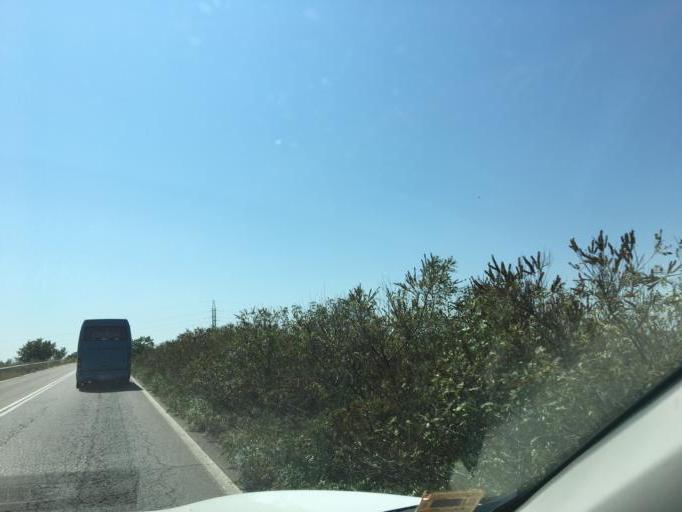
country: BG
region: Burgas
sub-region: Obshtina Kameno
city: Kameno
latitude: 42.5949
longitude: 27.3926
